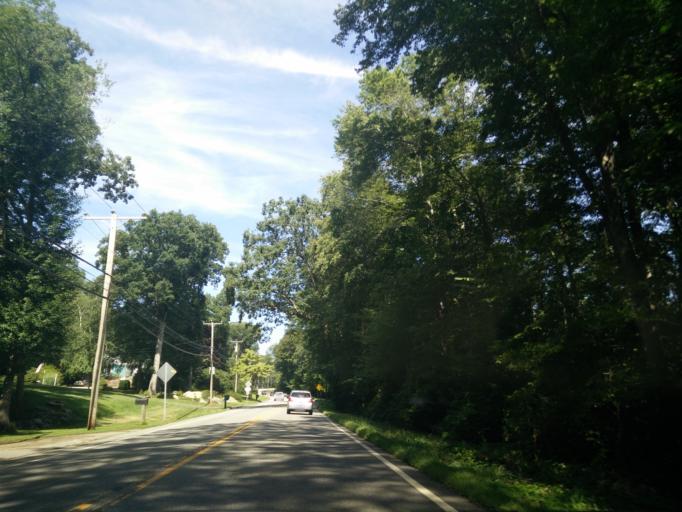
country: US
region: Connecticut
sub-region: Middlesex County
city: Clinton
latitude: 41.3065
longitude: -72.5358
